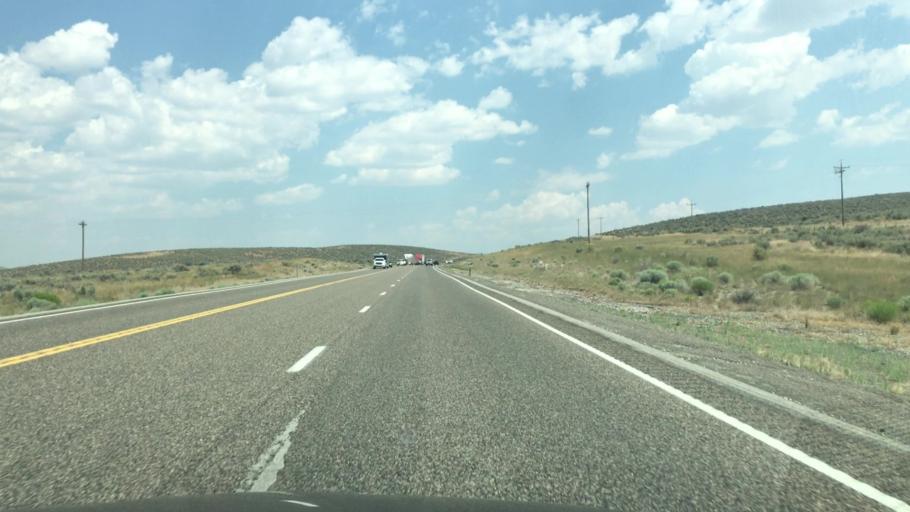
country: US
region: Nevada
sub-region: Elko County
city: Wells
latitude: 41.1826
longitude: -114.8755
